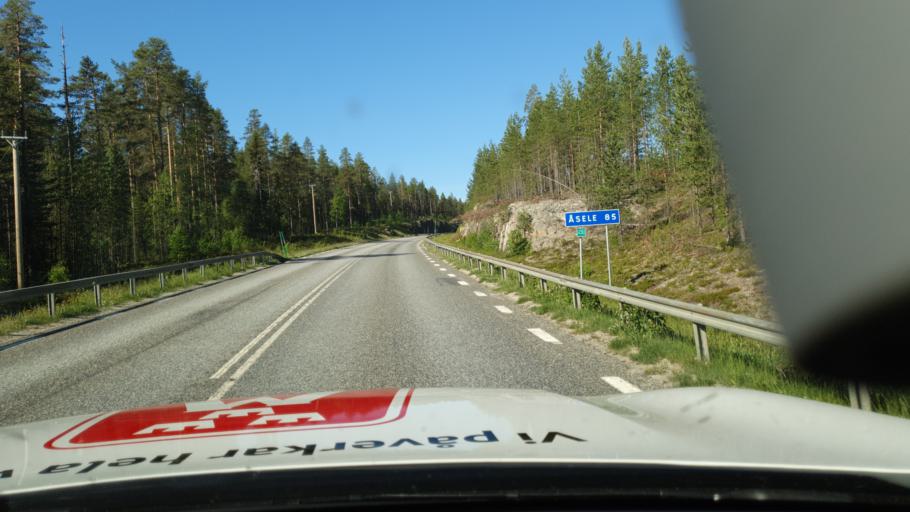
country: SE
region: Vaesterbotten
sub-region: Lycksele Kommun
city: Lycksele
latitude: 64.5749
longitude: 18.6501
